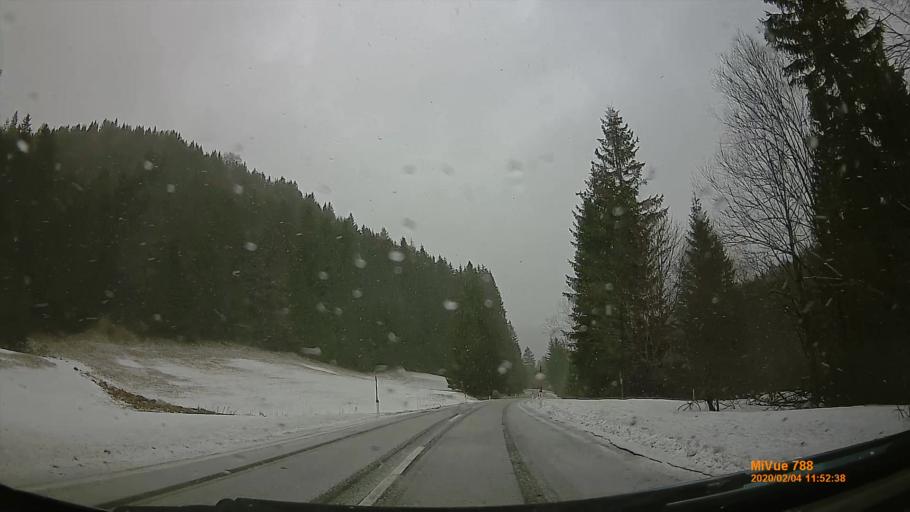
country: AT
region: Styria
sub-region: Politischer Bezirk Bruck-Muerzzuschlag
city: Muerzsteg
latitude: 47.7428
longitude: 15.4861
